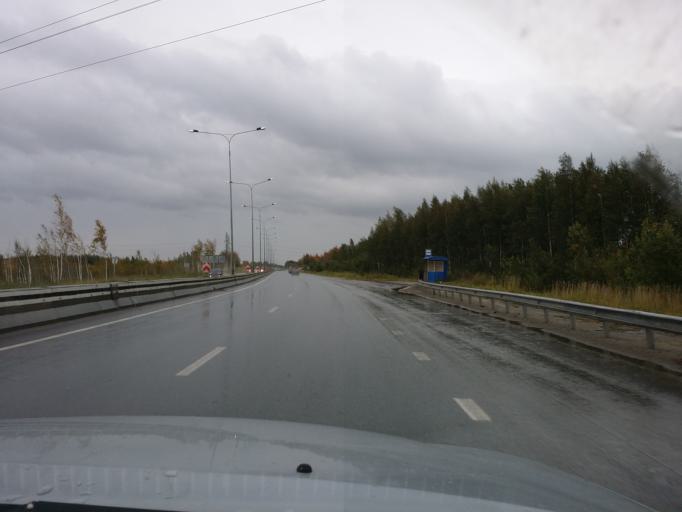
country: RU
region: Khanty-Mansiyskiy Avtonomnyy Okrug
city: Megion
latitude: 61.0481
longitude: 76.1307
